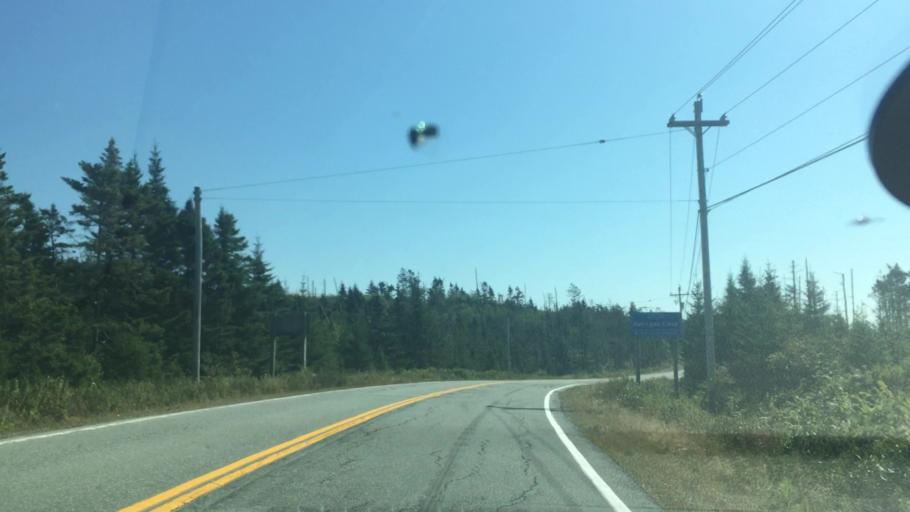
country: CA
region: Nova Scotia
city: New Glasgow
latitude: 44.9172
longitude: -62.3212
